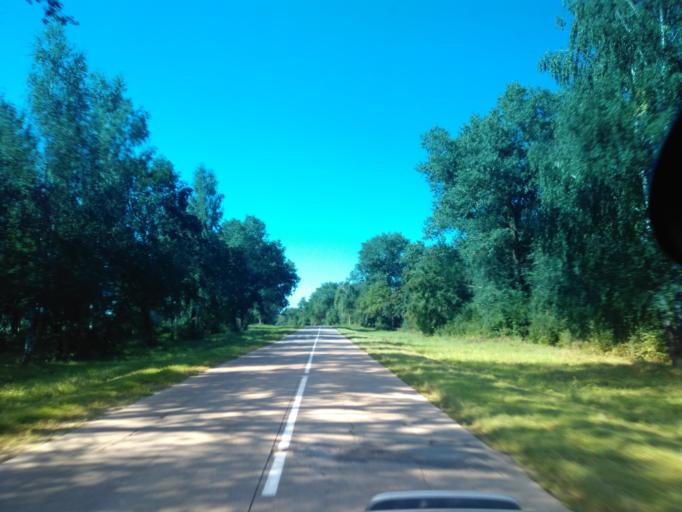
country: BY
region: Minsk
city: Stan'kava
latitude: 53.6443
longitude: 27.2956
